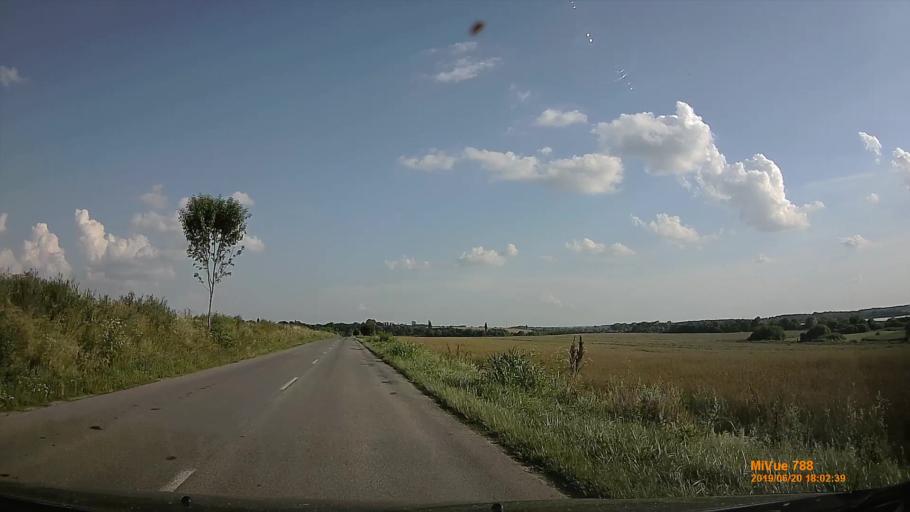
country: HU
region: Baranya
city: Szentlorinc
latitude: 46.0721
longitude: 17.9907
